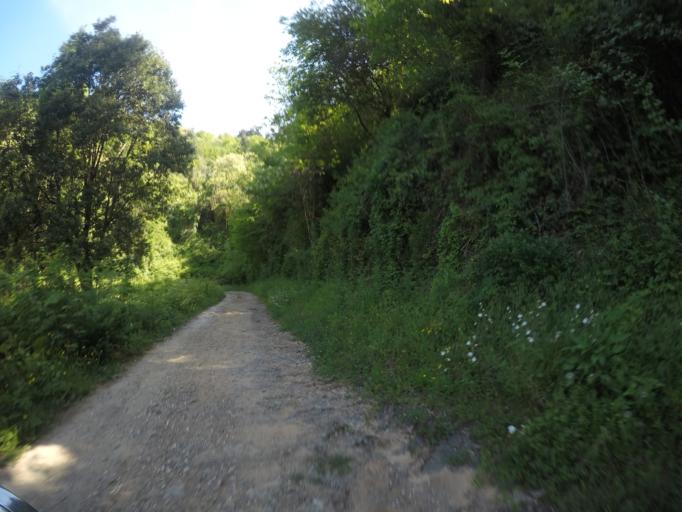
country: IT
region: Tuscany
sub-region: Provincia di Massa-Carrara
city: Massa
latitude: 44.0594
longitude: 10.1042
